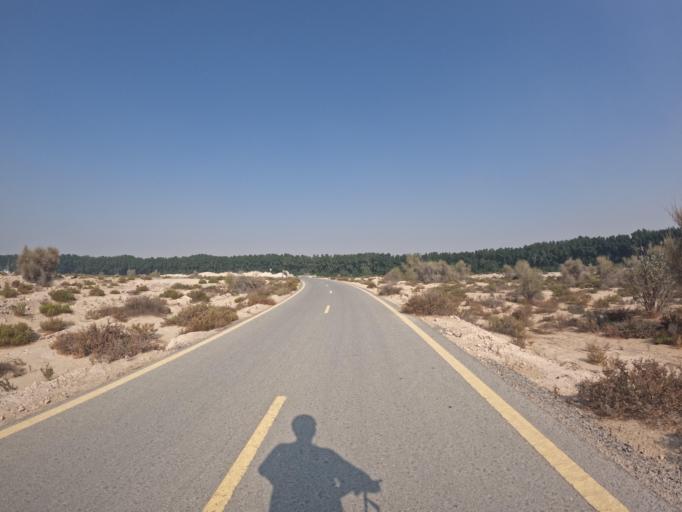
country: AE
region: Dubai
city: Dubai
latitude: 25.0964
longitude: 55.3276
